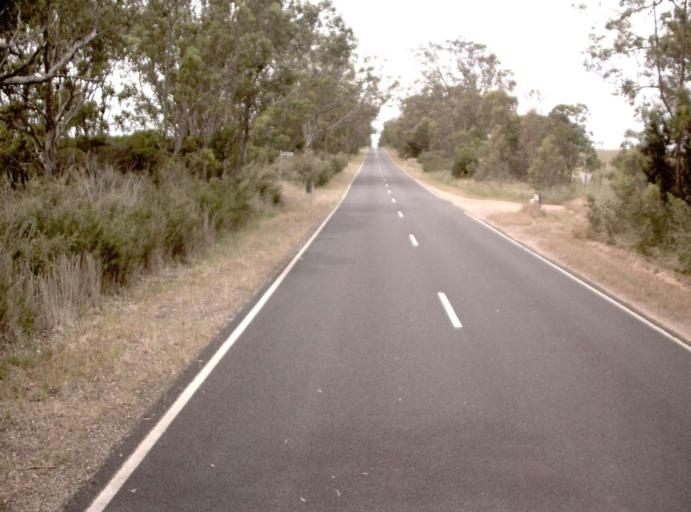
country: AU
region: Victoria
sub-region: Wellington
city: Sale
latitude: -37.9815
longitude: 147.1736
